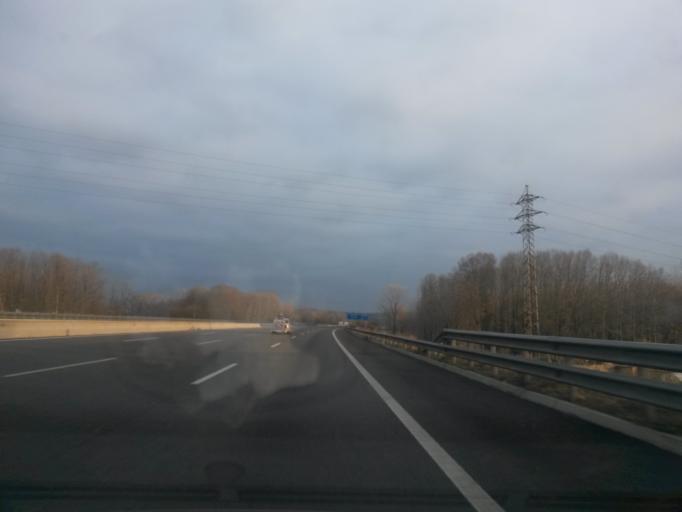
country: ES
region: Catalonia
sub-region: Provincia de Girona
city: Salt
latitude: 41.9768
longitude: 2.7791
